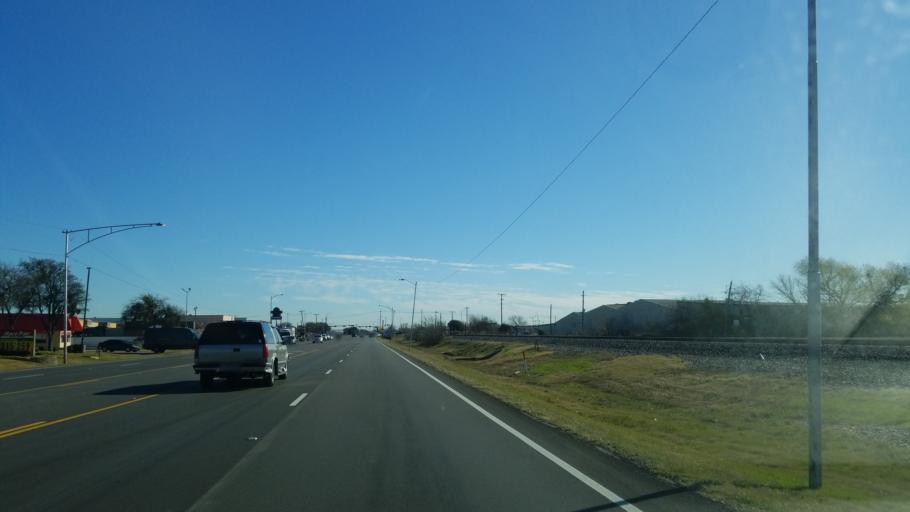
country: US
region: Texas
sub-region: Dallas County
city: Grand Prairie
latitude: 32.7402
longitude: -97.0499
